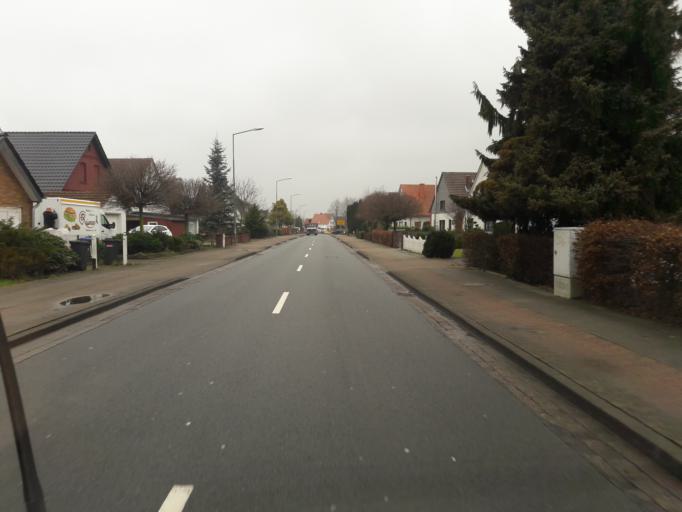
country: DE
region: North Rhine-Westphalia
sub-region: Regierungsbezirk Detmold
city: Minden
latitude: 52.3017
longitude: 8.8630
